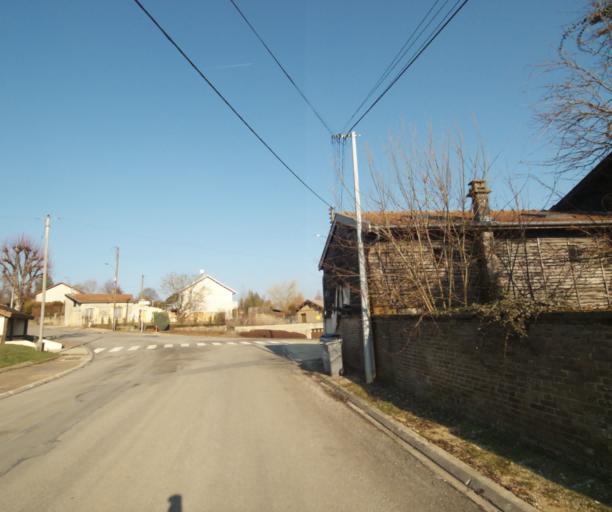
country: FR
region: Champagne-Ardenne
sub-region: Departement de la Haute-Marne
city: Wassy
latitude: 48.5135
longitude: 4.9169
